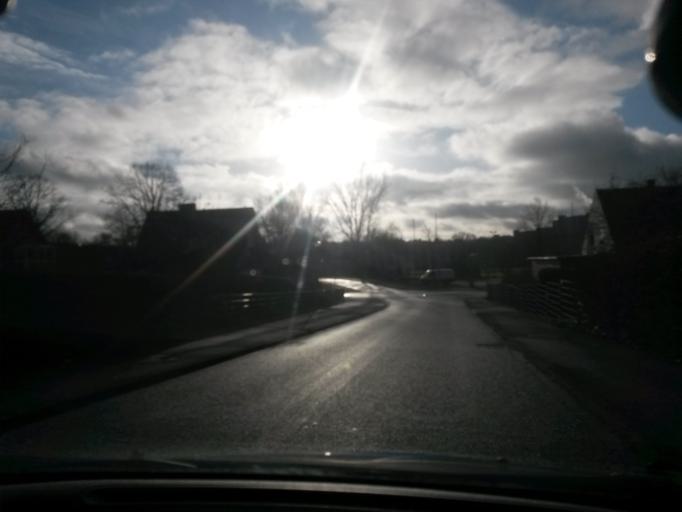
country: DE
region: Lower Saxony
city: Lueneburg
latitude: 53.2423
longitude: 10.4413
